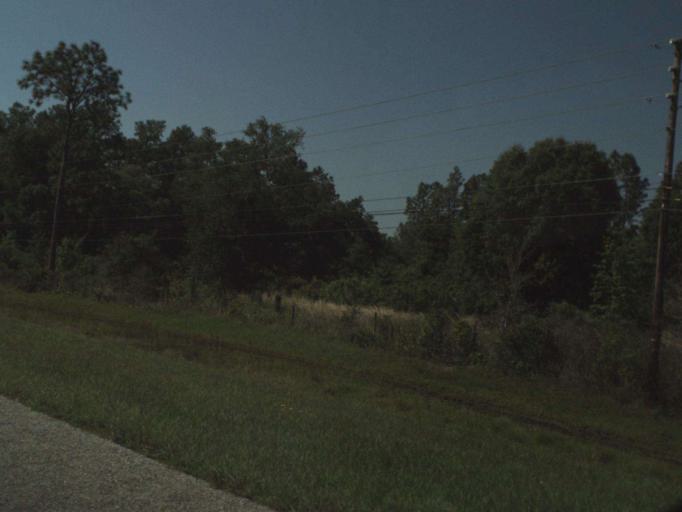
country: US
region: Florida
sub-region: Orange County
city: Wedgefield
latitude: 28.5012
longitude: -81.0508
